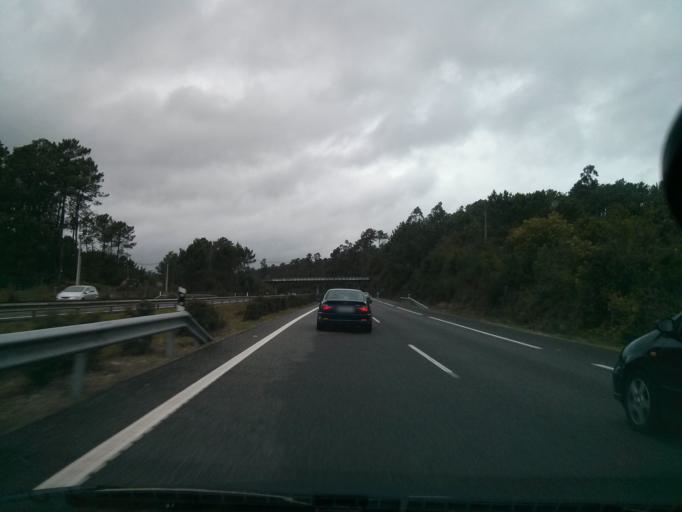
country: ES
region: Galicia
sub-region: Provincia de Pontevedra
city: Ponteareas
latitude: 42.1576
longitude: -8.5219
